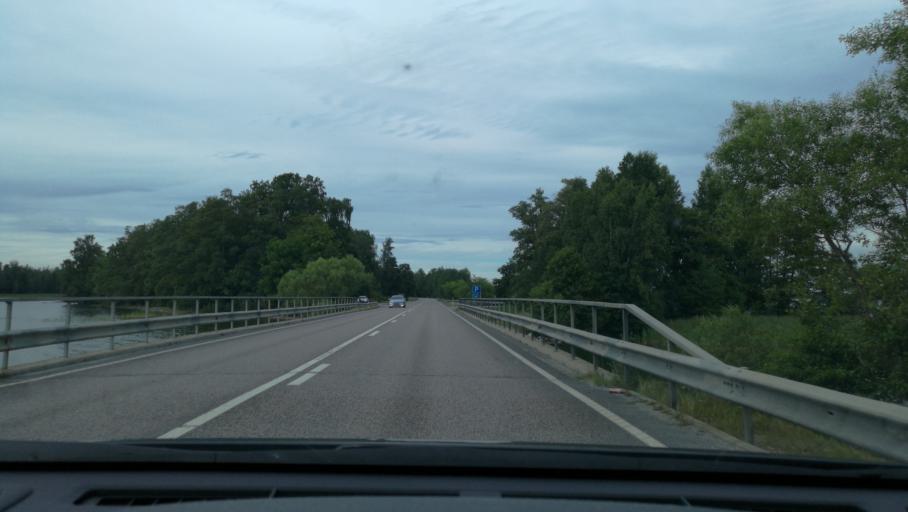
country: SE
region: Vaestmanland
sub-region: Kungsors Kommun
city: Kungsoer
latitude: 59.2469
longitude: 16.1046
